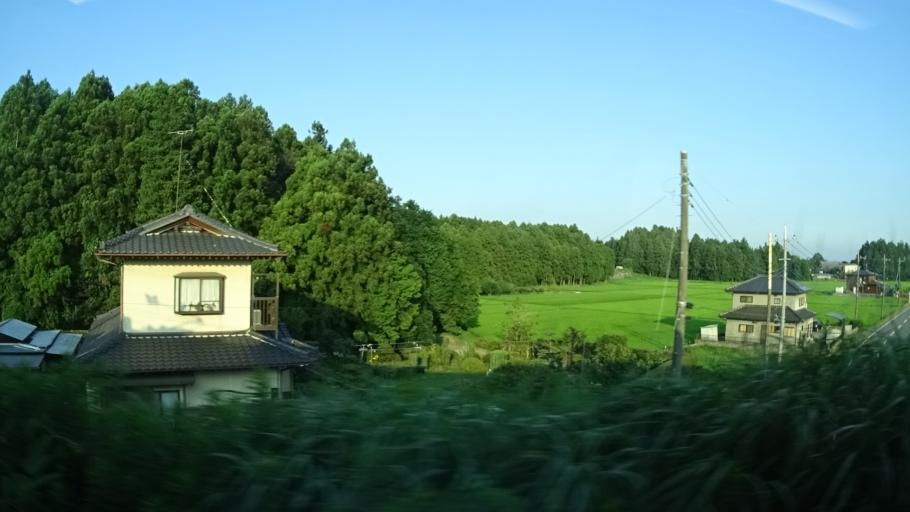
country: JP
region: Ibaraki
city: Tomobe
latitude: 36.3312
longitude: 140.2954
